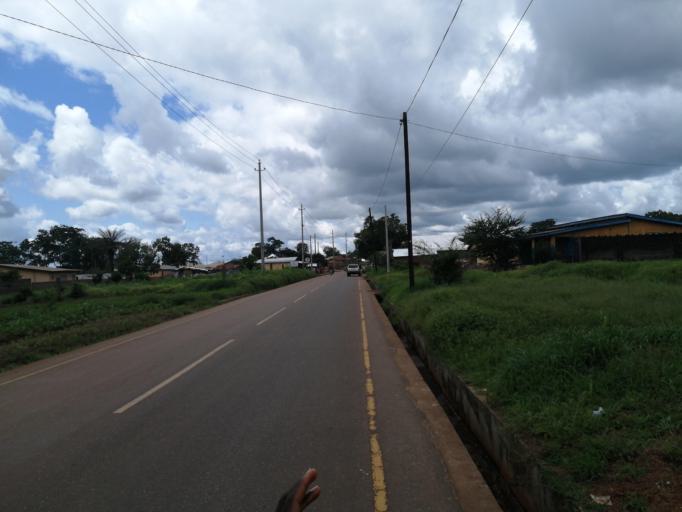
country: SL
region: Northern Province
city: Port Loko
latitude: 8.7721
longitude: -12.7763
